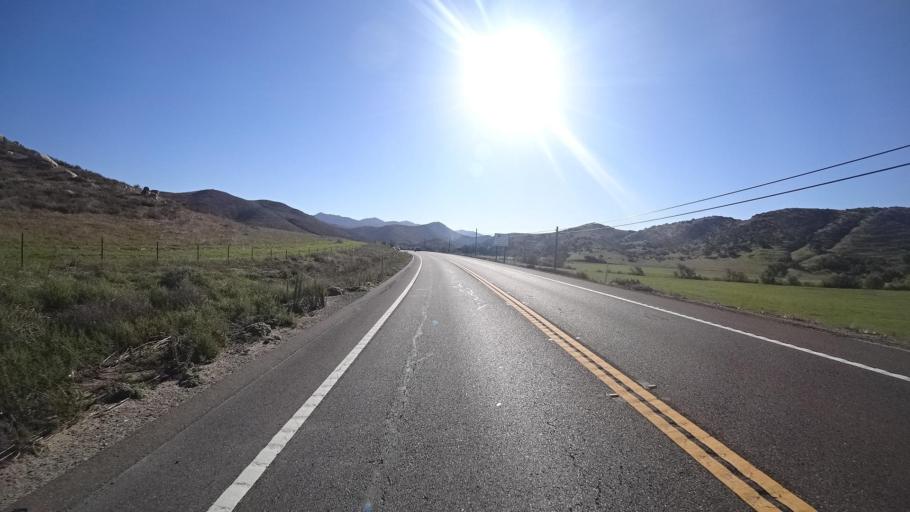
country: US
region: California
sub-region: San Diego County
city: Jamul
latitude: 32.6709
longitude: -116.8318
